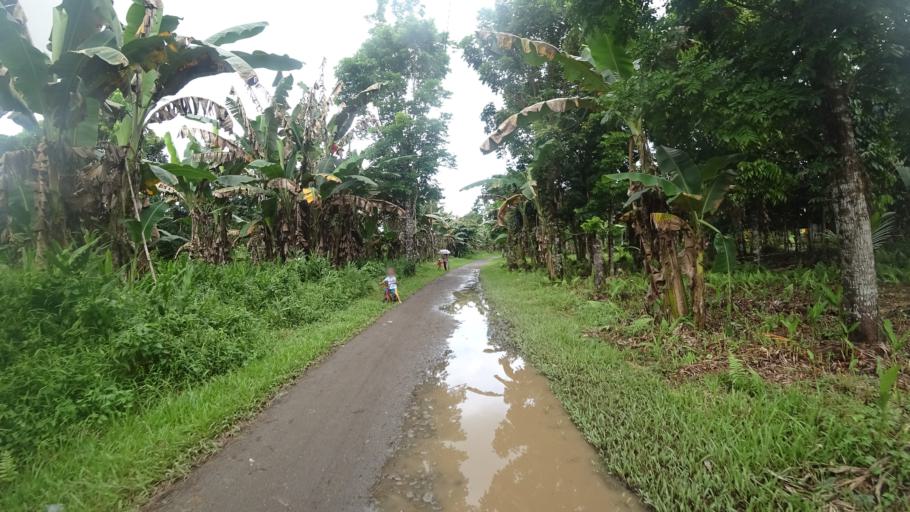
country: PH
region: Eastern Visayas
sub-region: Province of Leyte
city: Alangalang
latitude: 11.1642
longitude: 124.8521
